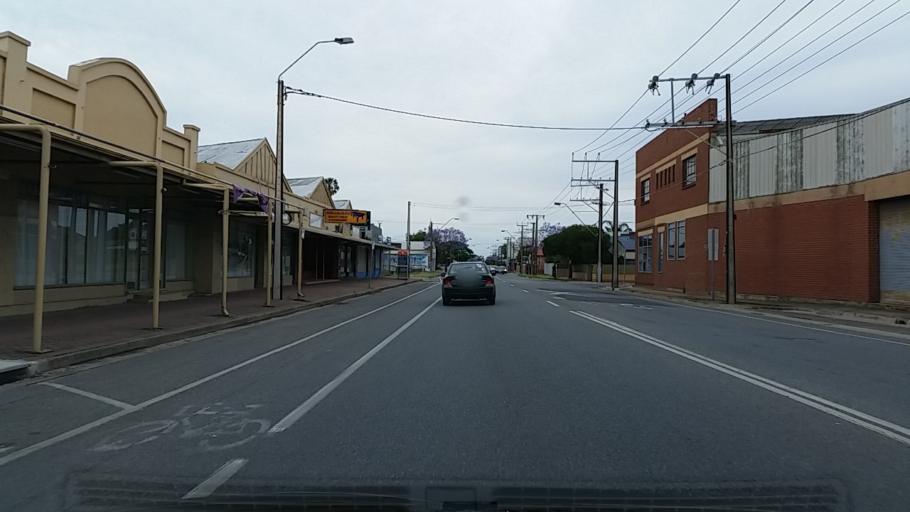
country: AU
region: South Australia
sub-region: Charles Sturt
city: Woodville
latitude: -34.8853
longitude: 138.5490
